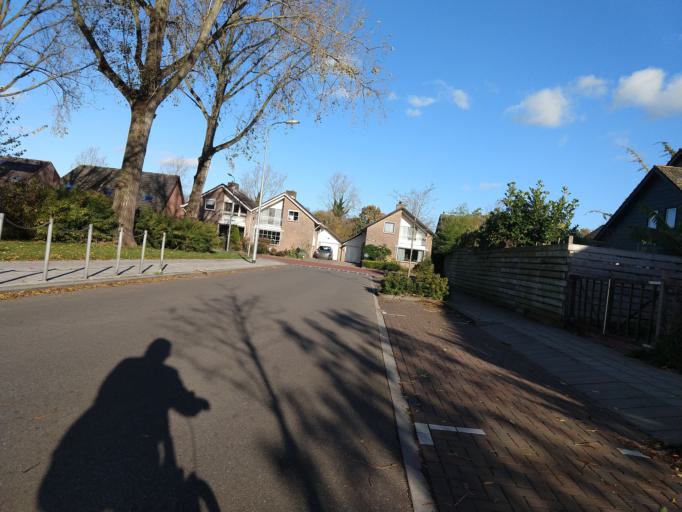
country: NL
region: Zeeland
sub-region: Gemeente Middelburg
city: Middelburg
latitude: 51.4949
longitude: 3.6265
